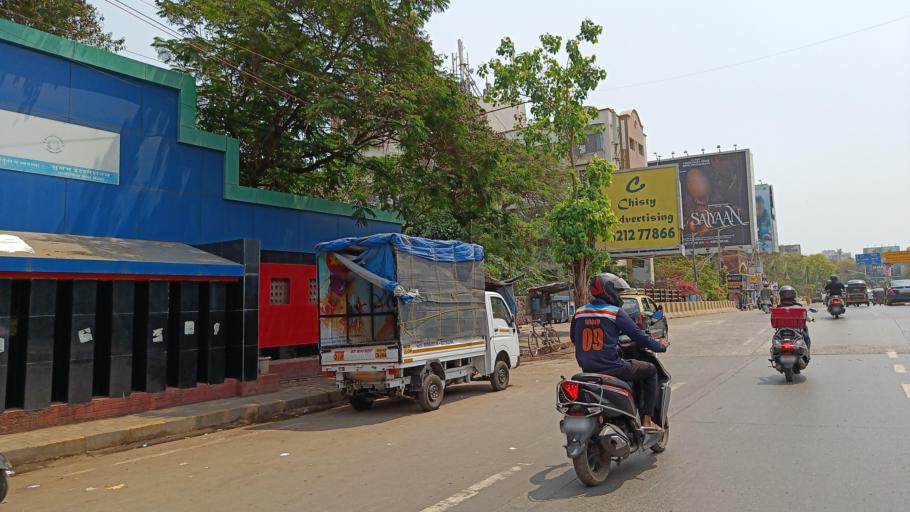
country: IN
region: Maharashtra
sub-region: Mumbai Suburban
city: Mumbai
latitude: 19.0855
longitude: 72.8300
